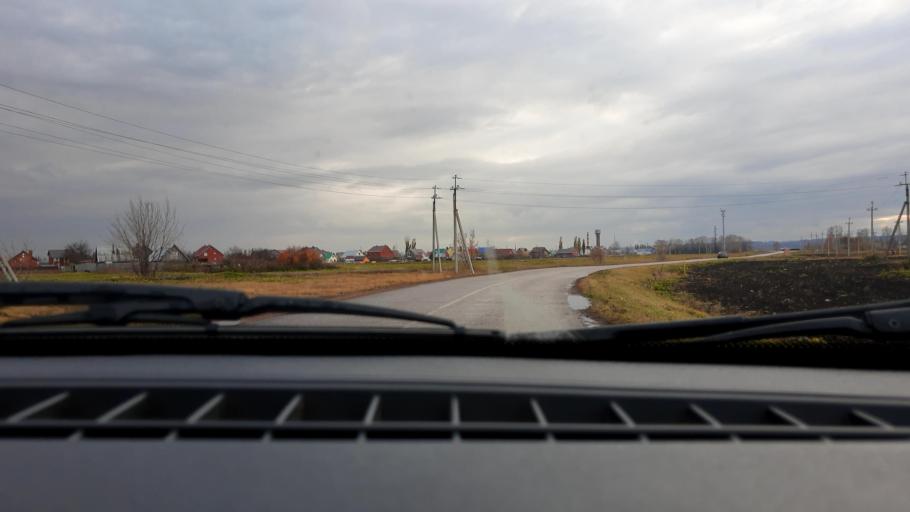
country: RU
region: Bashkortostan
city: Ufa
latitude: 54.8478
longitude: 56.0094
